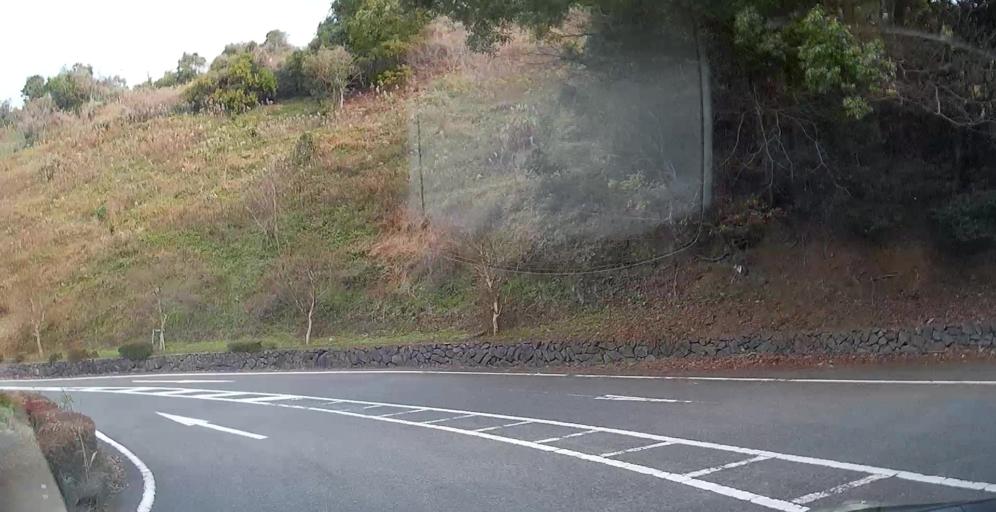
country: JP
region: Kumamoto
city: Minamata
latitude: 32.3261
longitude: 130.4745
